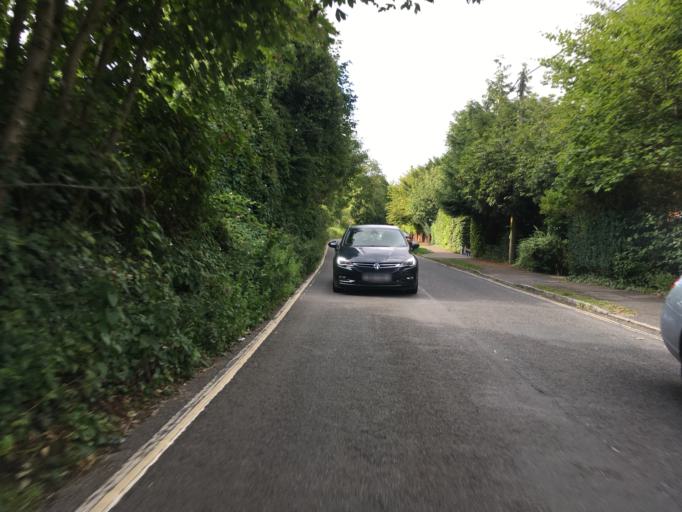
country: GB
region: England
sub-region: Hampshire
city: Compton
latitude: 51.0232
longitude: -1.3298
